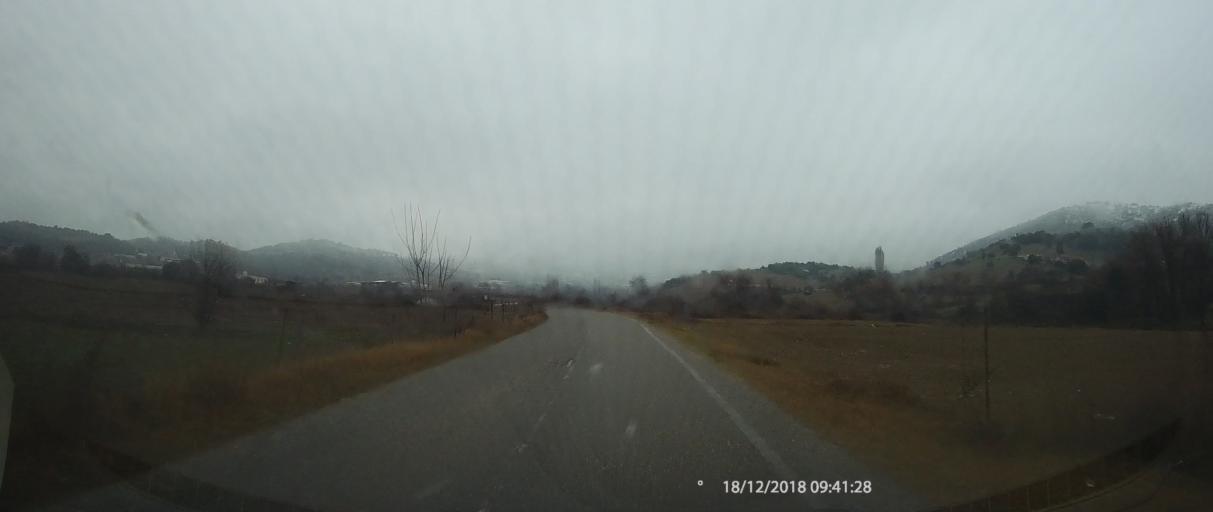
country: GR
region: Thessaly
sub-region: Nomos Larisis
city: Elassona
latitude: 40.0118
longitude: 22.2323
